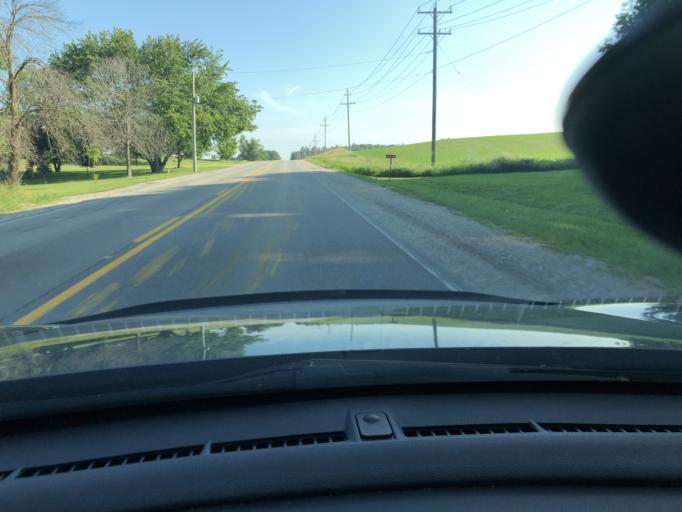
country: CA
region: Ontario
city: Stratford
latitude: 43.3894
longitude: -80.8373
